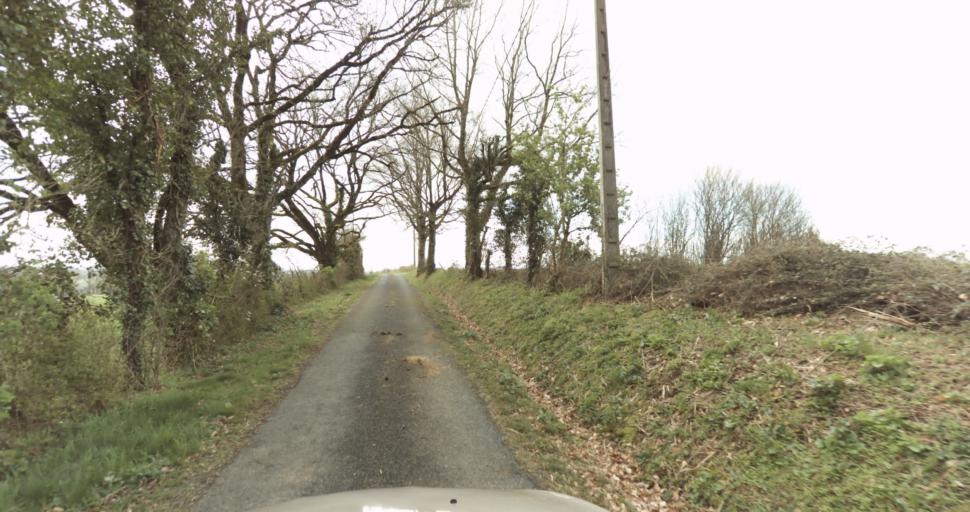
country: FR
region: Midi-Pyrenees
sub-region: Departement du Tarn
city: Frejairolles
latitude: 43.8579
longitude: 2.2189
